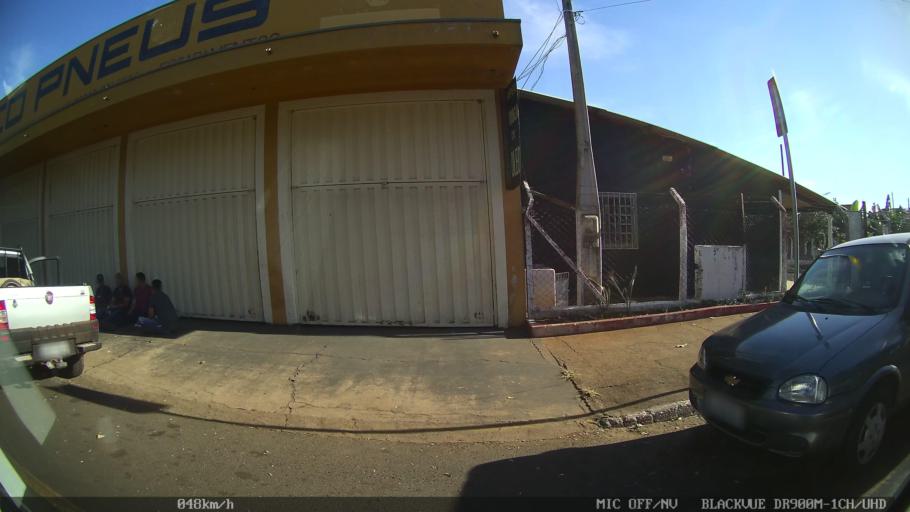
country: BR
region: Sao Paulo
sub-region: Franca
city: Franca
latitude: -20.5156
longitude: -47.3854
